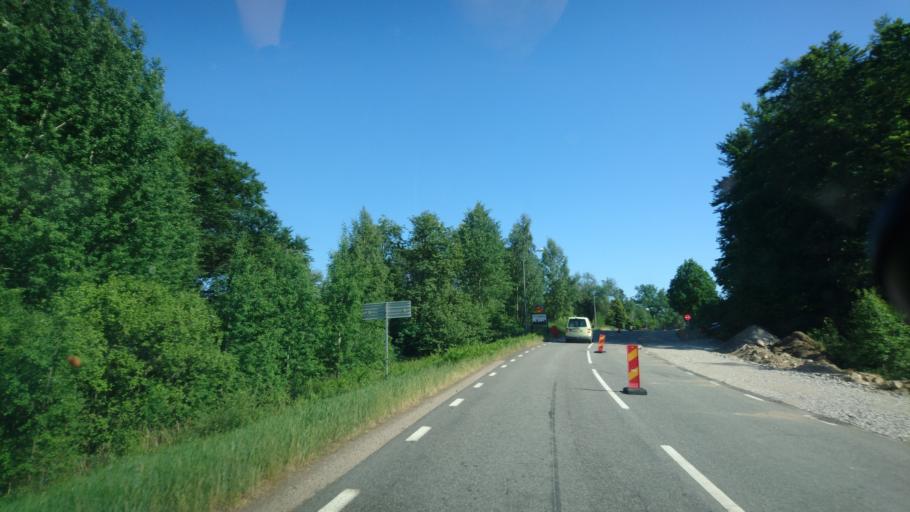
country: SE
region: Skane
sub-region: Osby Kommun
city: Lonsboda
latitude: 56.4069
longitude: 14.3168
